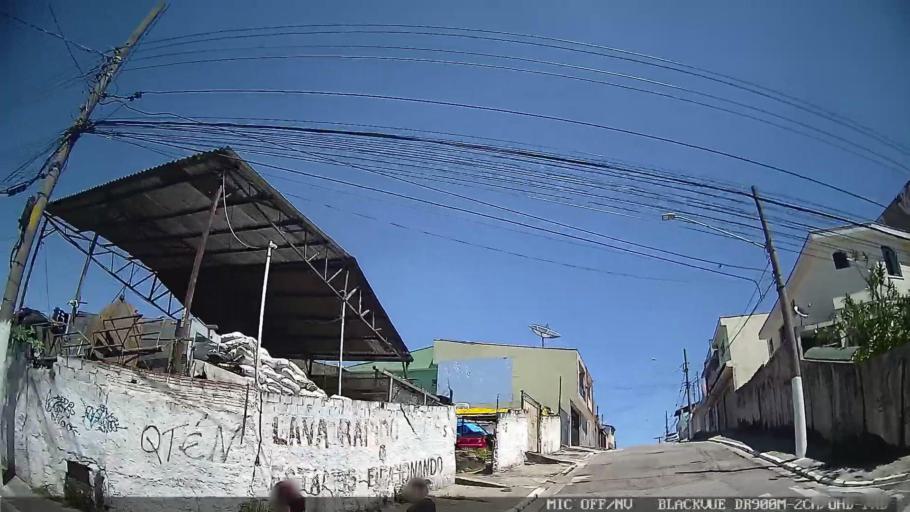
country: BR
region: Sao Paulo
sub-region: Sao Caetano Do Sul
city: Sao Caetano do Sul
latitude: -23.5861
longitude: -46.5262
